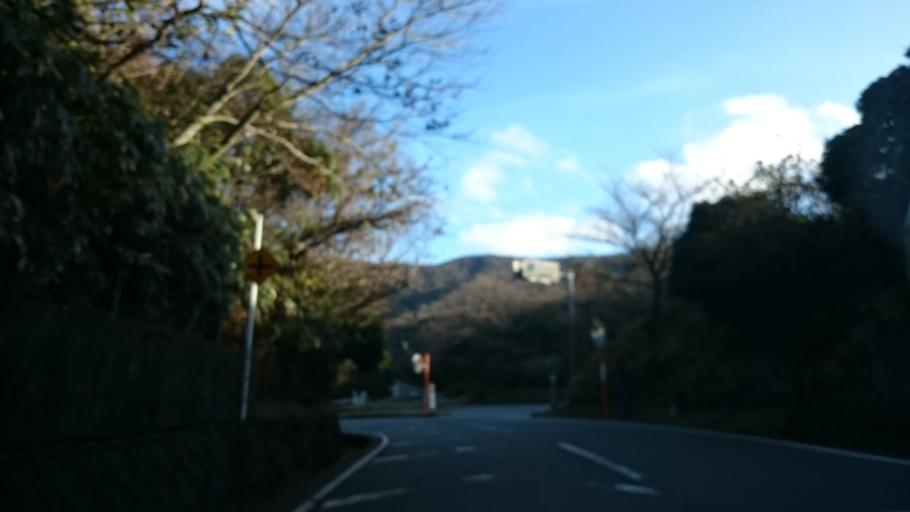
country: JP
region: Shizuoka
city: Heda
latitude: 34.9716
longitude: 138.8365
